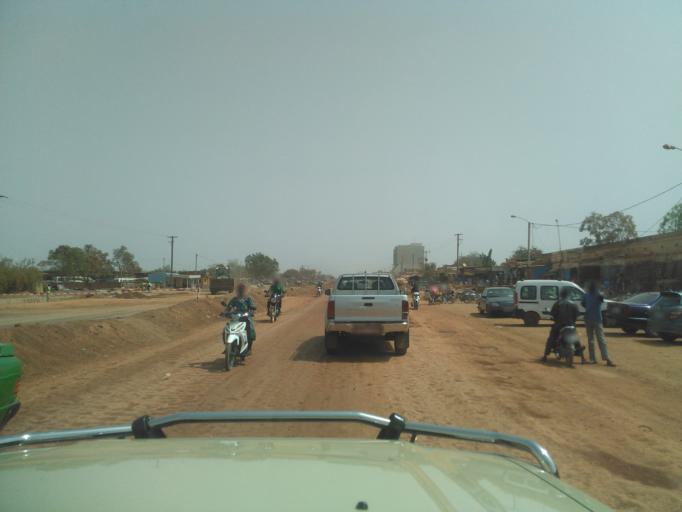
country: BF
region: Centre
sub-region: Kadiogo Province
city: Ouagadougou
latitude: 12.3907
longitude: -1.4782
